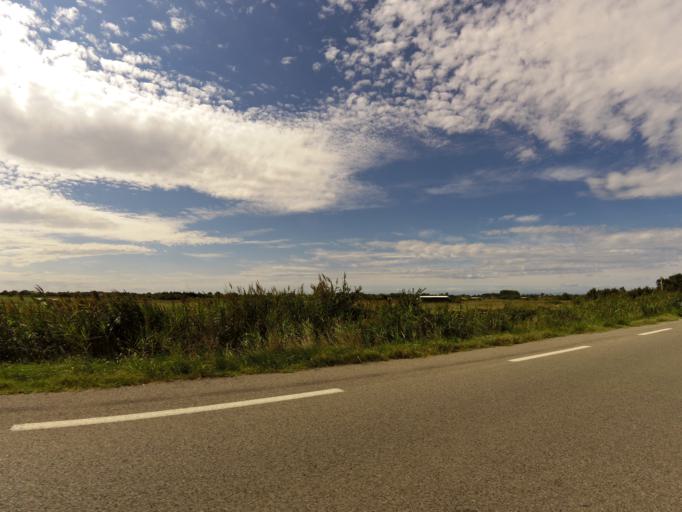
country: FR
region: Languedoc-Roussillon
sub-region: Departement de l'Herault
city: Marsillargues
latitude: 43.6193
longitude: 4.1916
